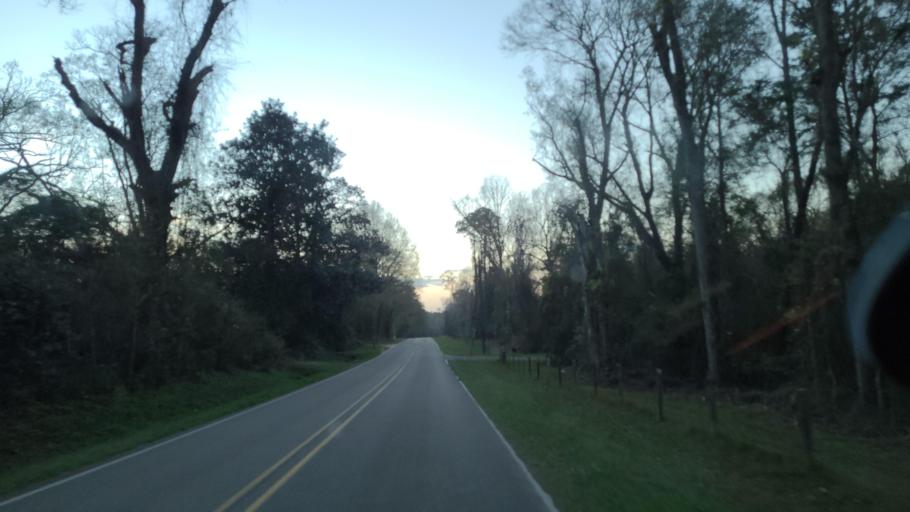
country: US
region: Mississippi
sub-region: Forrest County
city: Hattiesburg
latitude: 31.1676
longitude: -89.2275
